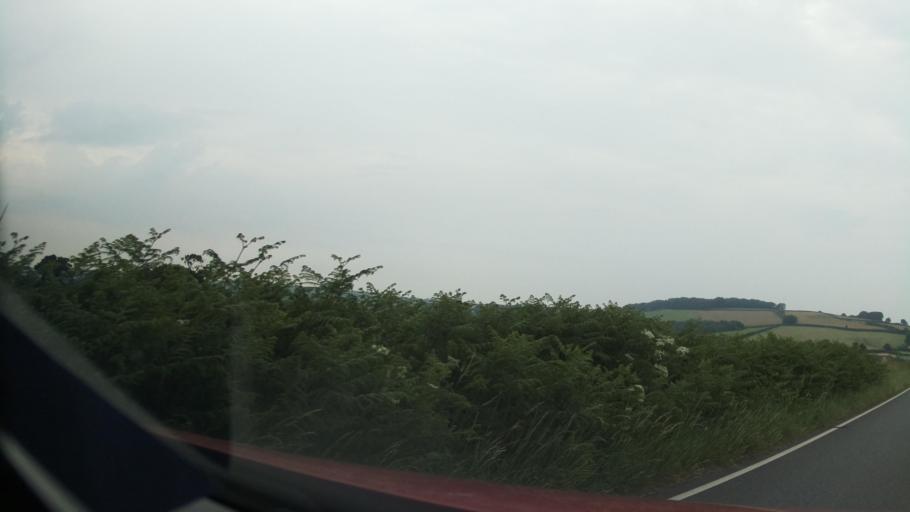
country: GB
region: England
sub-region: Dorset
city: Beaminster
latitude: 50.8382
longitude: -2.7769
